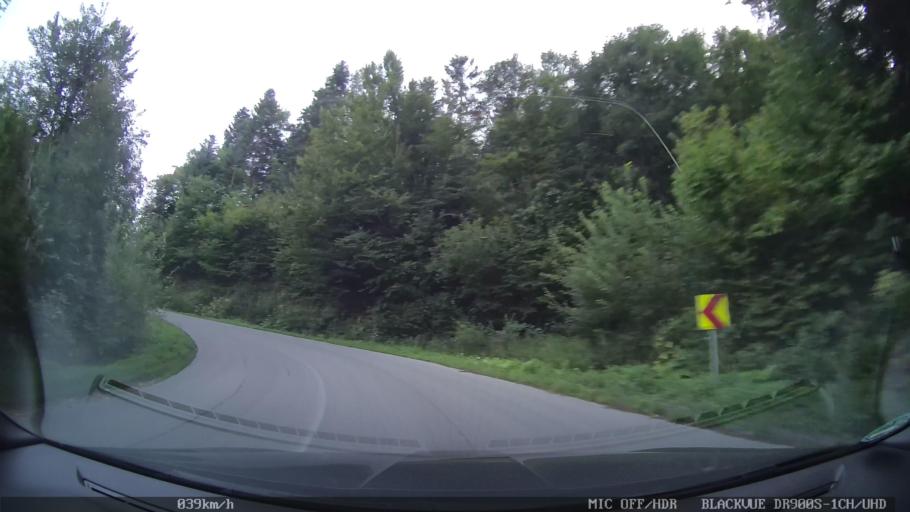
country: HR
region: Primorsko-Goranska
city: Vrbovsko
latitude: 45.2080
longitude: 15.0291
